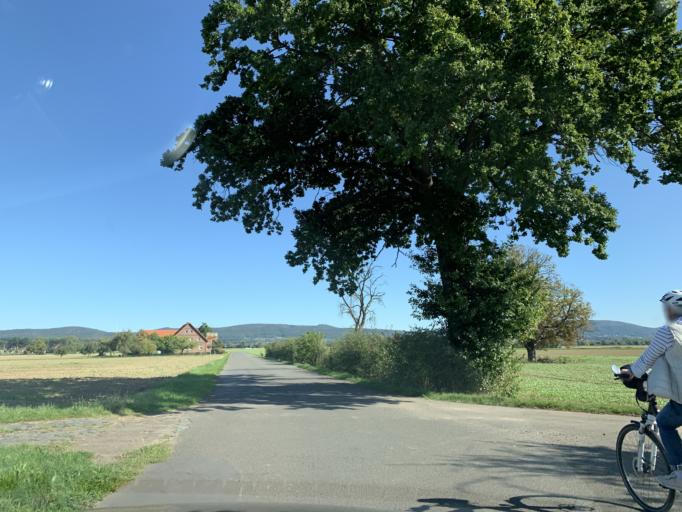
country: DE
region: North Rhine-Westphalia
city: Porta Westfalica
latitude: 52.1895
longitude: 8.9782
